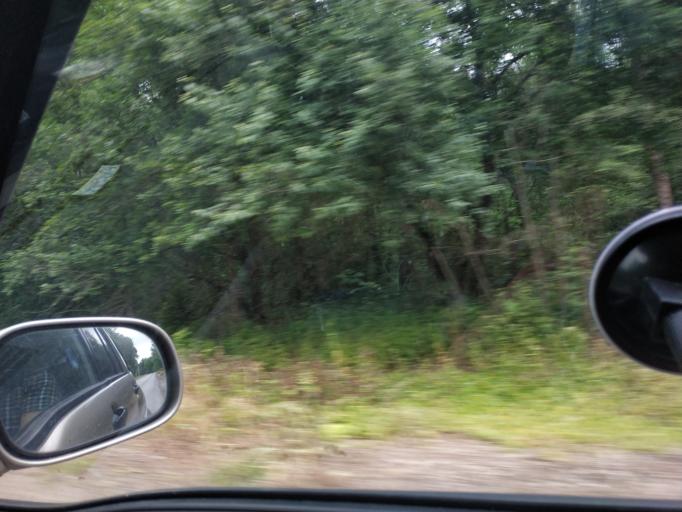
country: RU
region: Moskovskaya
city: Krasnoarmeysk
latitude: 56.0776
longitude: 38.2438
